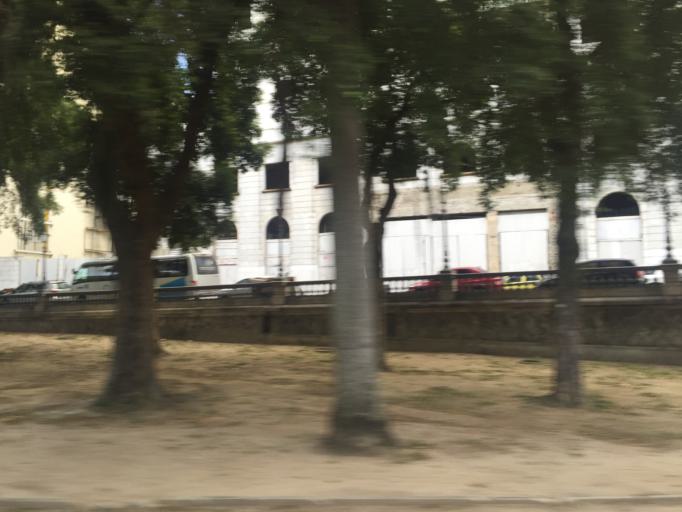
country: BR
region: Rio de Janeiro
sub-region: Rio De Janeiro
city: Rio de Janeiro
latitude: -22.9227
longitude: -43.1724
